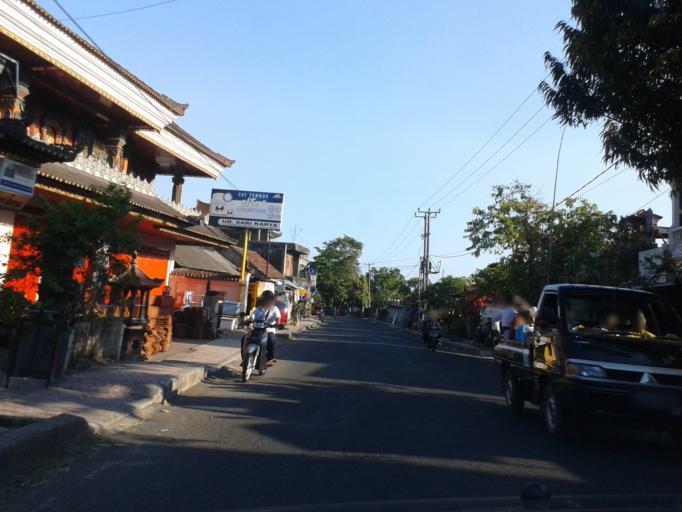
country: ID
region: Bali
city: Klungkung
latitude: -8.5204
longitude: 115.4012
